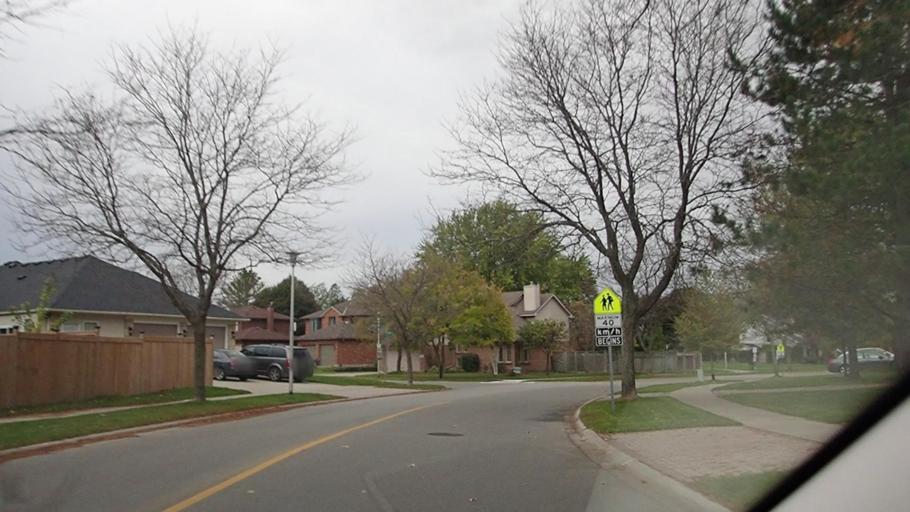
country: CA
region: Ontario
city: London
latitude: 43.0358
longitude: -81.2649
